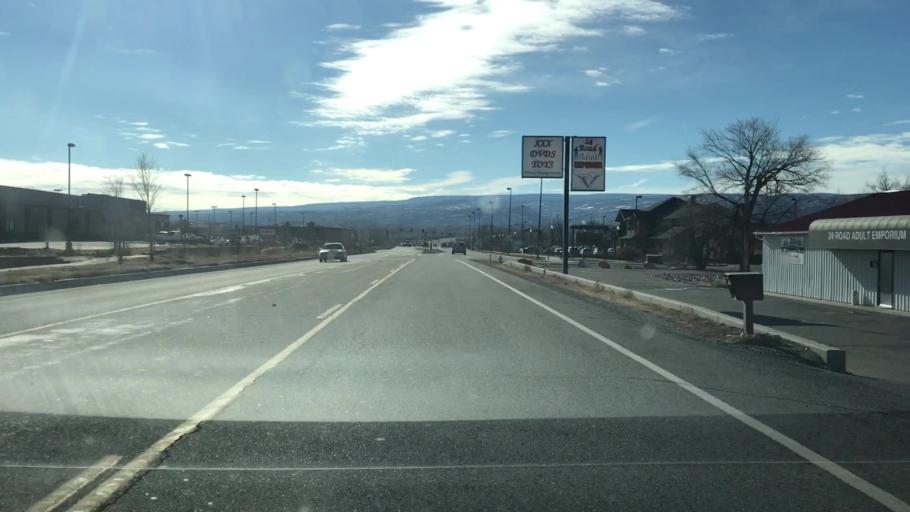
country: US
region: Colorado
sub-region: Mesa County
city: Redlands
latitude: 39.0979
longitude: -108.6082
